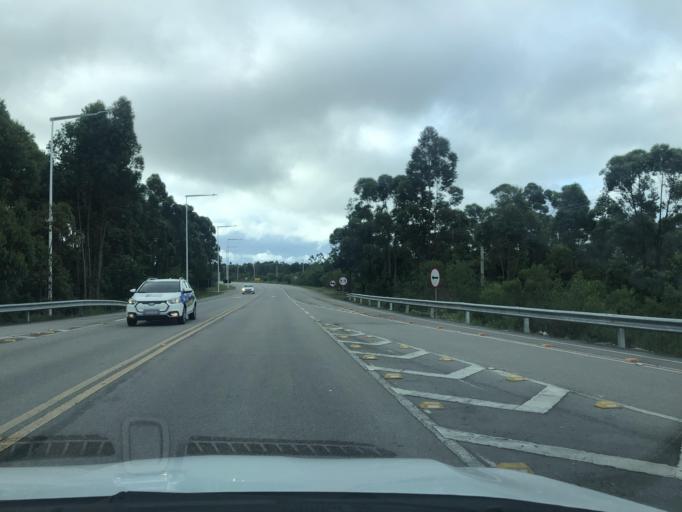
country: BR
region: Santa Catarina
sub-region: Florianopolis
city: Tapera
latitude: -27.6802
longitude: -48.5357
